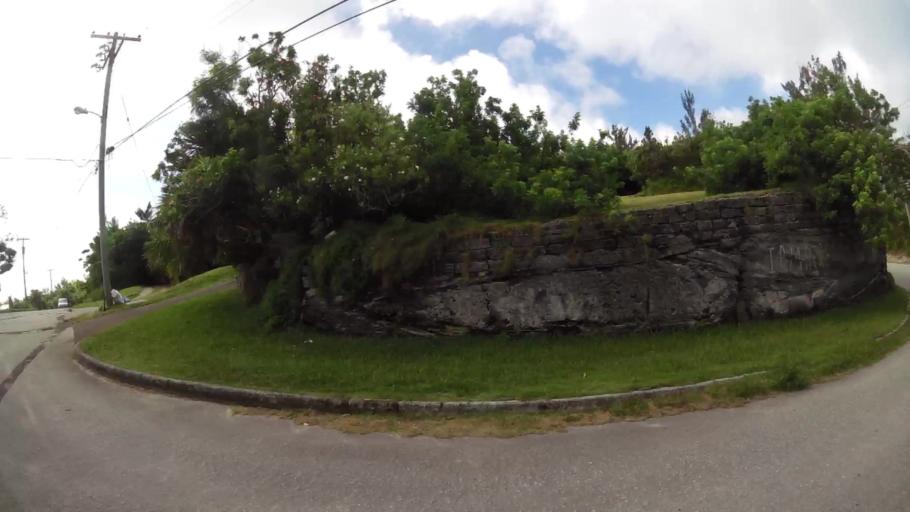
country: BM
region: Saint George
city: Saint George
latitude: 32.3853
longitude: -64.6759
